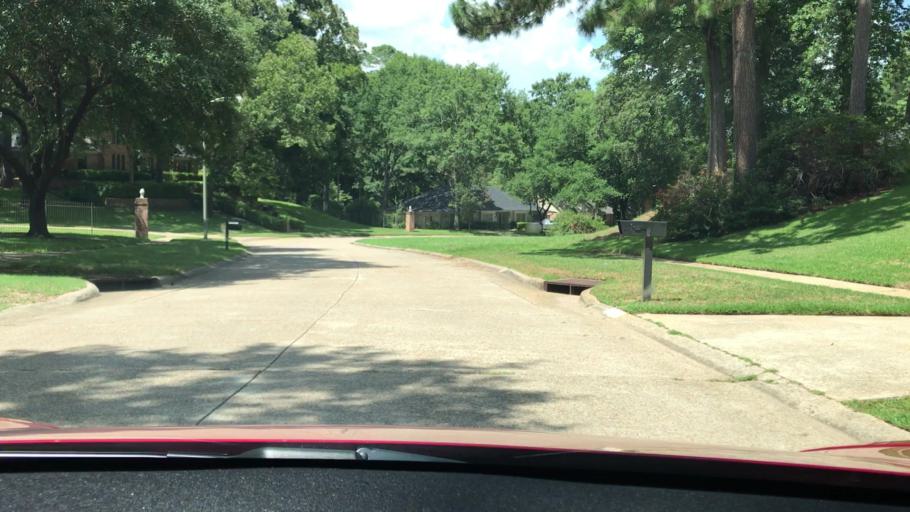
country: US
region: Louisiana
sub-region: Bossier Parish
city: Bossier City
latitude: 32.4254
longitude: -93.7315
